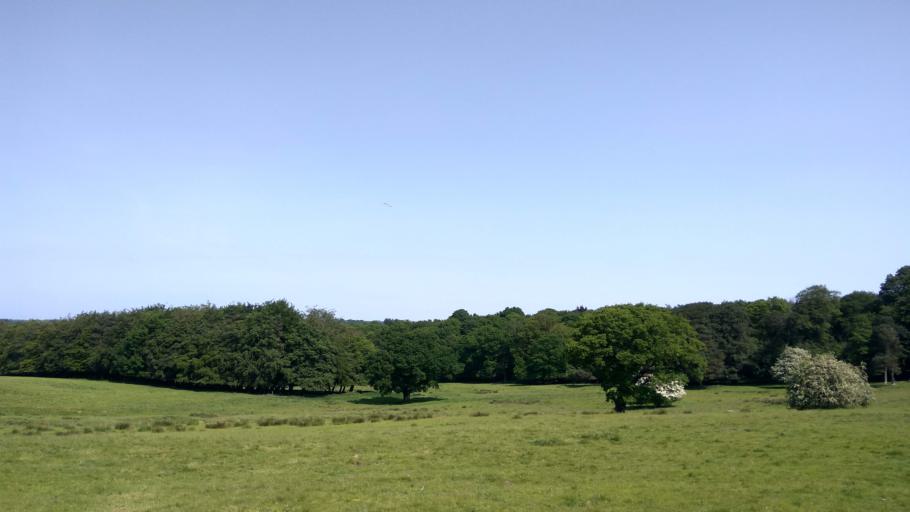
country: GB
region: England
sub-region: City and Borough of Leeds
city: Shadwell
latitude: 53.8833
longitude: -1.5105
